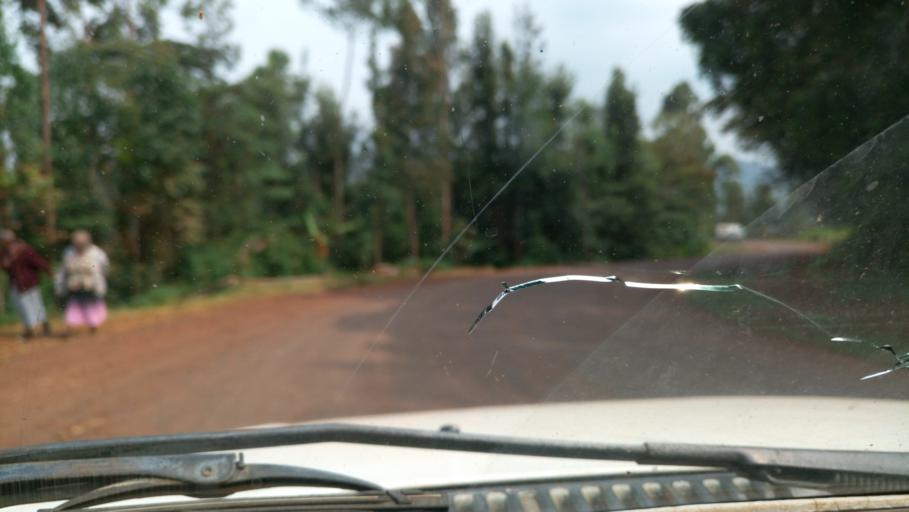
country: KE
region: Murang'a District
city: Kangema
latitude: -0.6297
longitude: 37.0230
